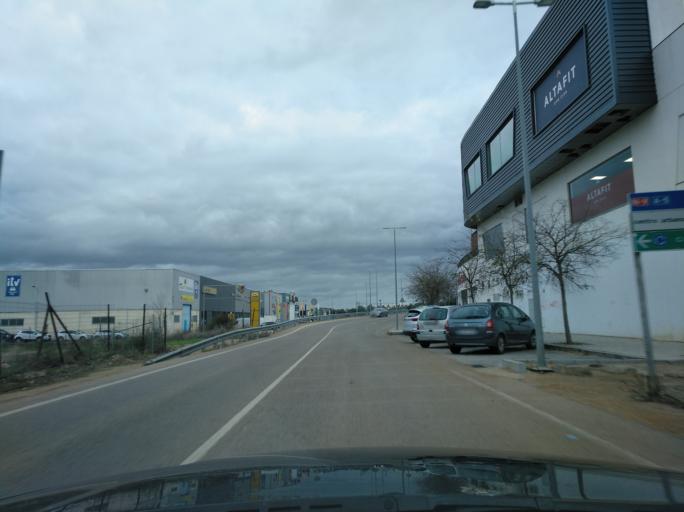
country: ES
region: Extremadura
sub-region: Provincia de Badajoz
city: Badajoz
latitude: 38.8789
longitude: -6.9468
